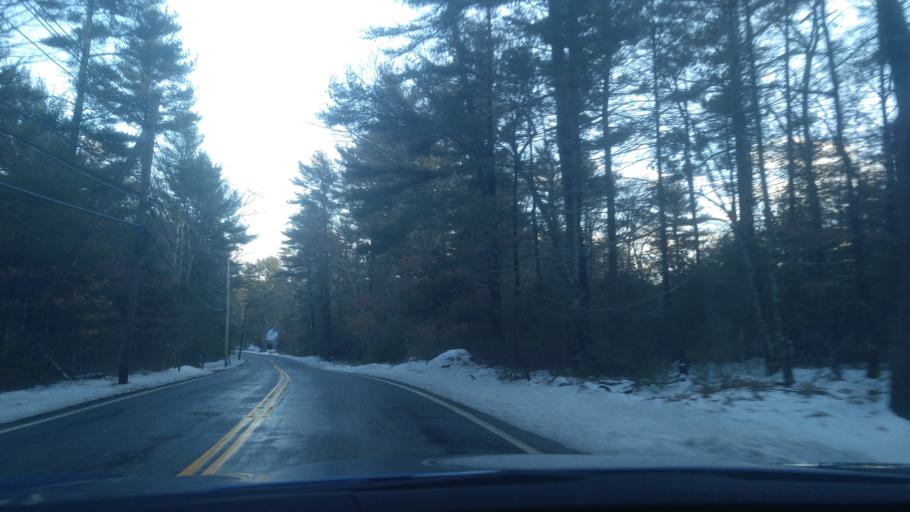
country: US
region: Rhode Island
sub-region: Kent County
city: West Greenwich
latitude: 41.6824
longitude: -71.6163
